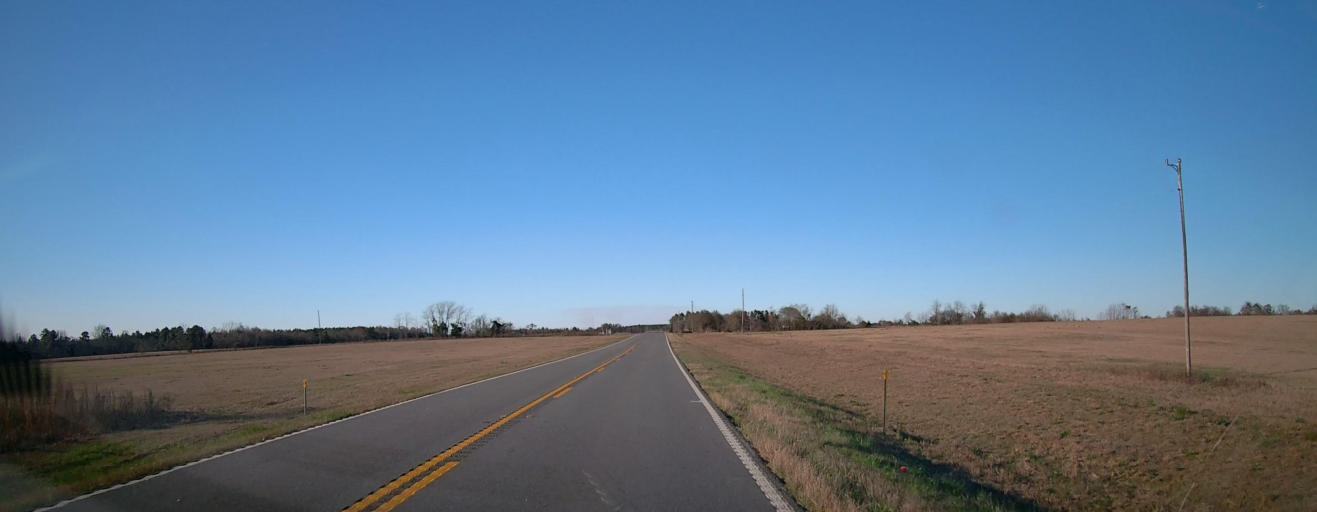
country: US
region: Georgia
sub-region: Talbot County
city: Talbotton
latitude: 32.5372
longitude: -84.4349
